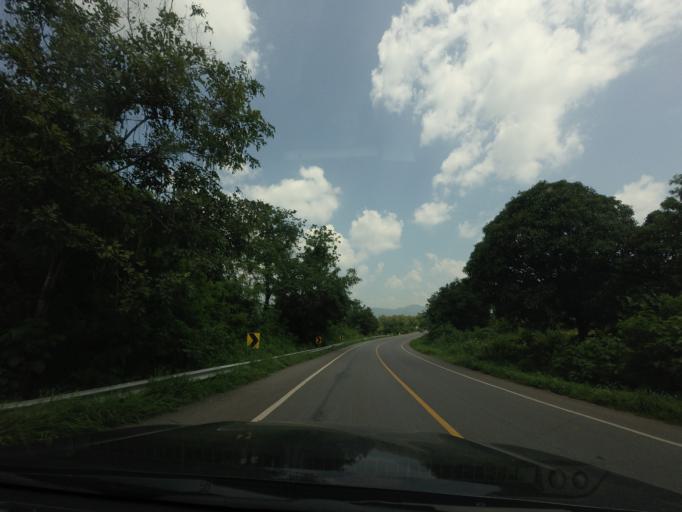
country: TH
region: Phitsanulok
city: Chat Trakan
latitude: 17.3086
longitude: 100.4777
